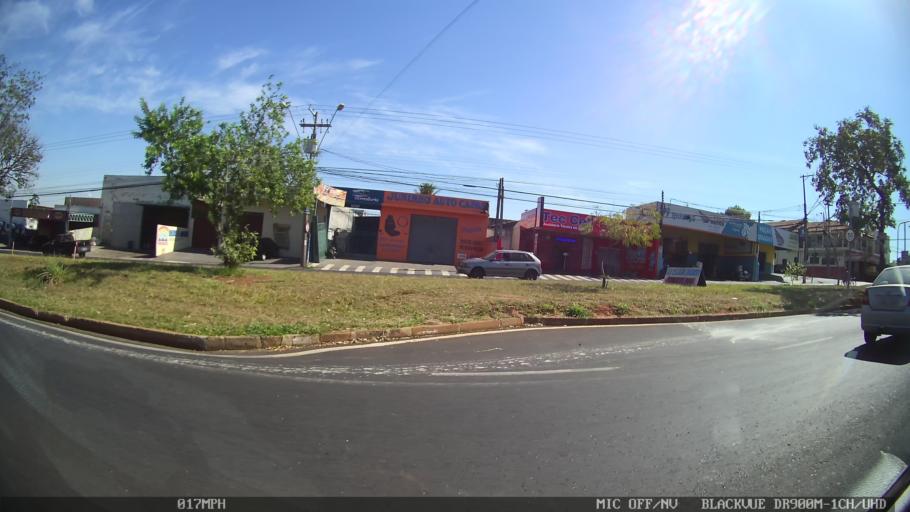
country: BR
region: Sao Paulo
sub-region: Sao Jose Do Rio Preto
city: Sao Jose do Rio Preto
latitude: -20.7749
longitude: -49.3854
